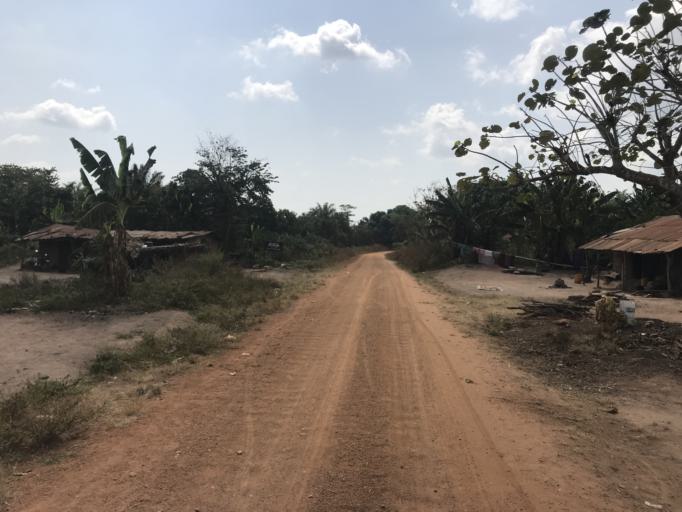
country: NG
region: Osun
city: Ifon
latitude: 7.9701
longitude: 4.5083
